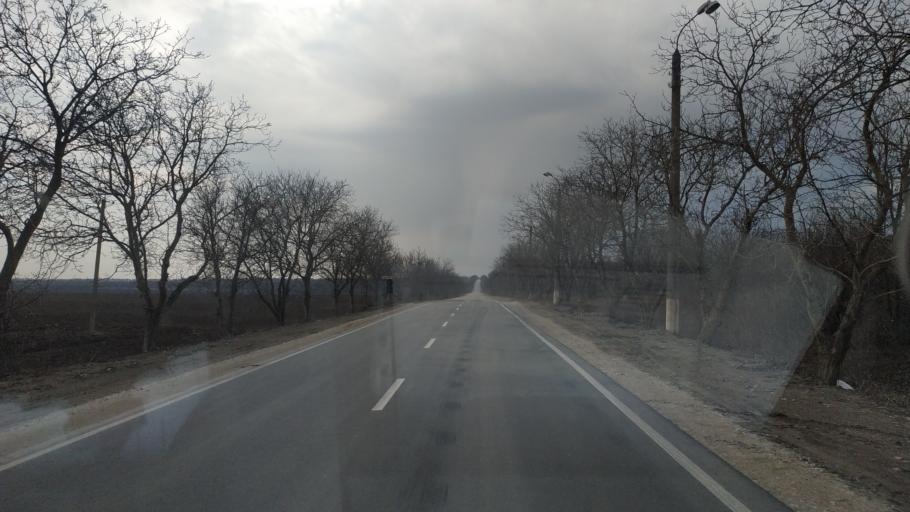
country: MD
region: Telenesti
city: Grigoriopol
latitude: 47.0195
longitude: 29.2900
